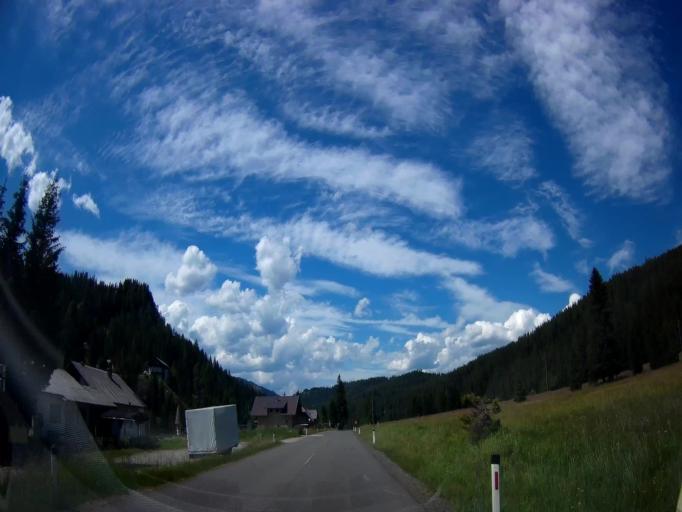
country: AT
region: Carinthia
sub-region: Politischer Bezirk Sankt Veit an der Glan
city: Glodnitz
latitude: 46.9532
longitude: 14.0255
